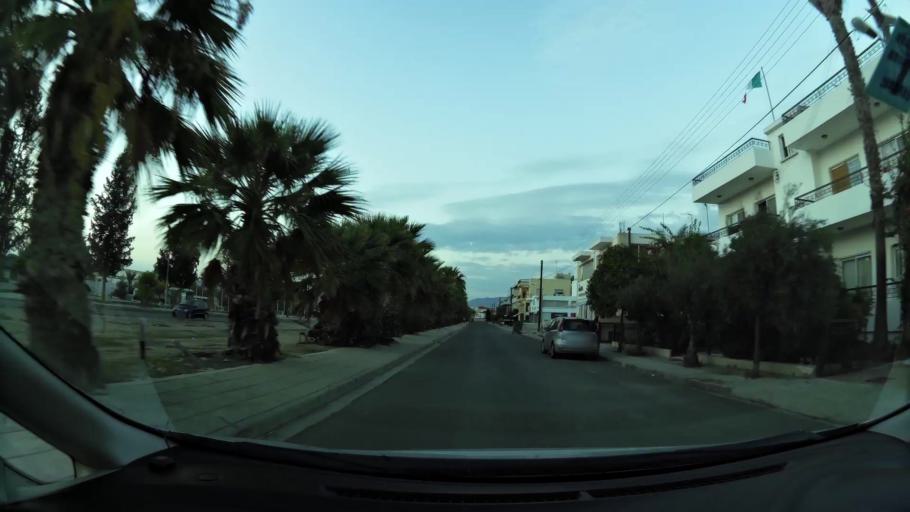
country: CY
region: Lefkosia
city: Nicosia
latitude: 35.1493
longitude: 33.3176
